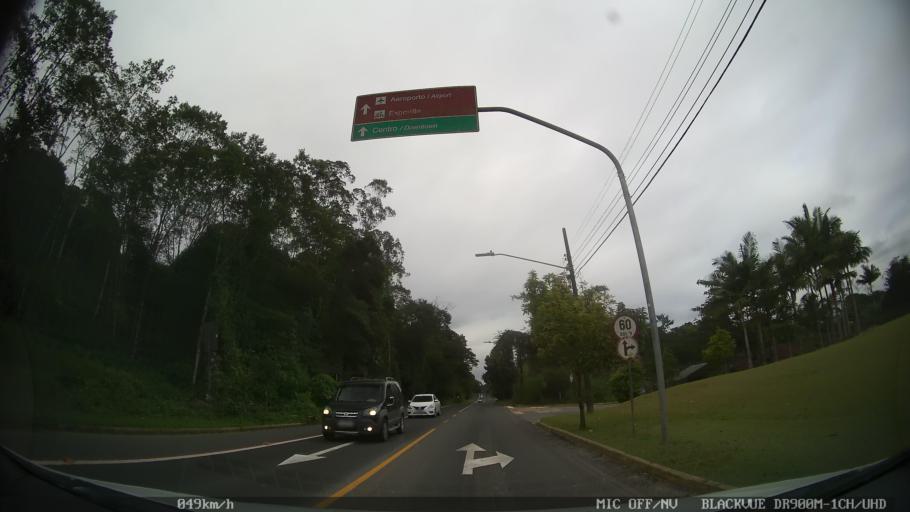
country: BR
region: Santa Catarina
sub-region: Joinville
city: Joinville
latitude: -26.3114
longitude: -48.8633
